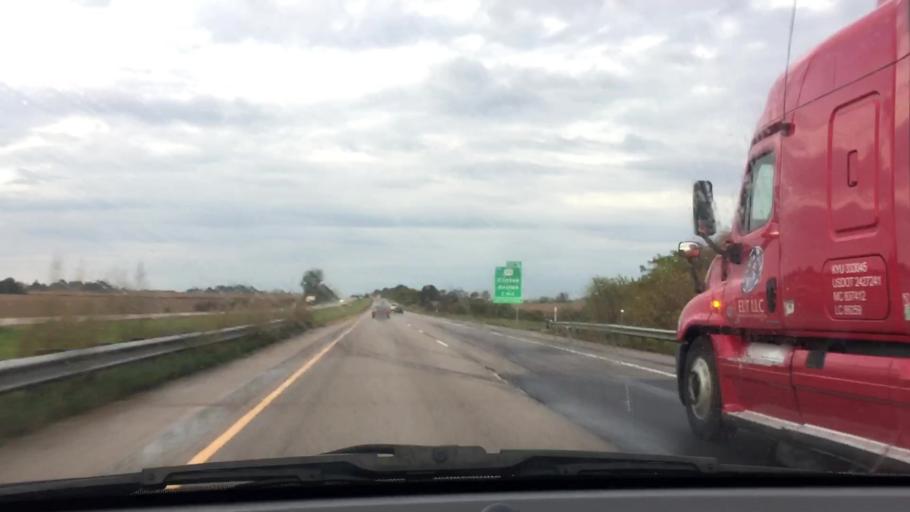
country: US
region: Wisconsin
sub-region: Rock County
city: Clinton
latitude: 42.5724
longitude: -88.8363
